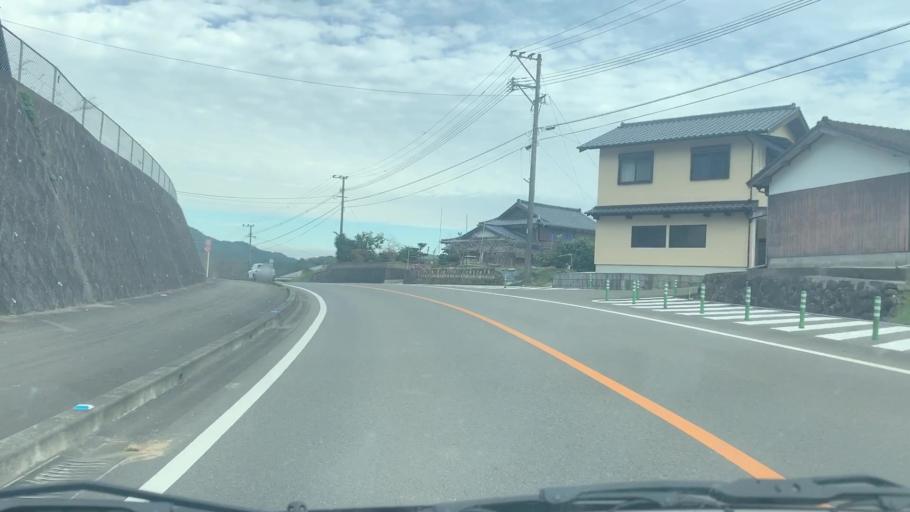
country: JP
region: Saga Prefecture
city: Takeocho-takeo
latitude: 33.2440
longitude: 129.9701
